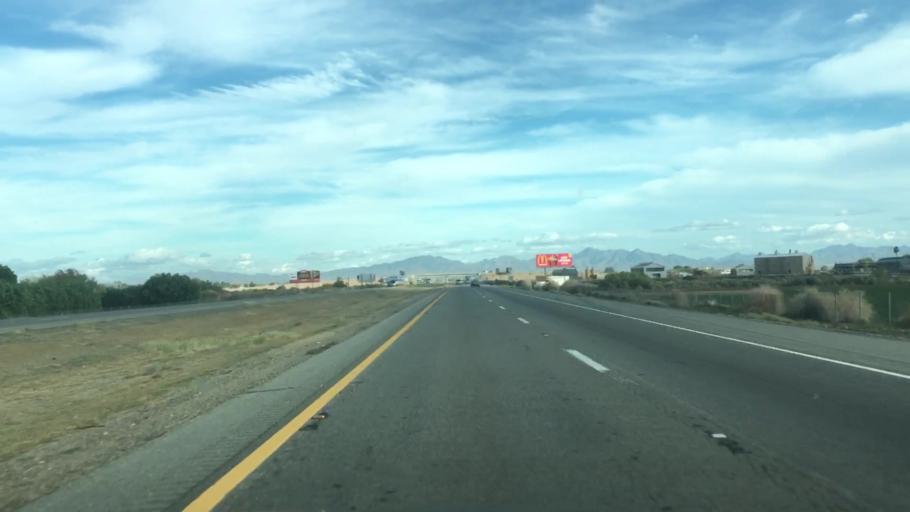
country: US
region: California
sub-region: Riverside County
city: Blythe
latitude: 33.6065
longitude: -114.6488
